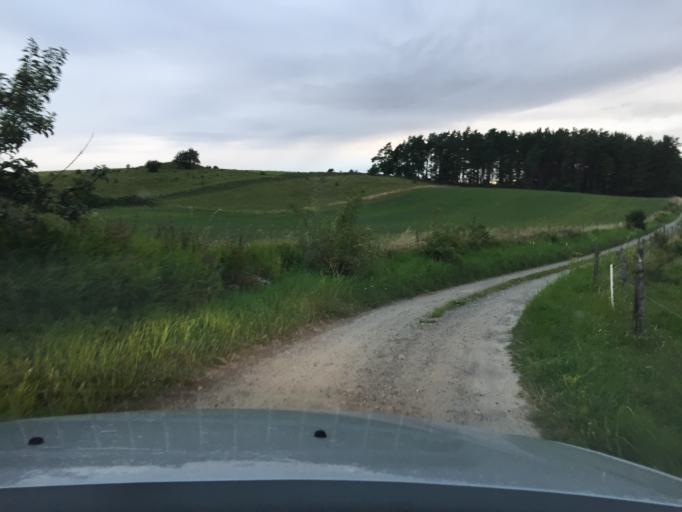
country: SE
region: Skane
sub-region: Kristianstads Kommun
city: Degeberga
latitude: 55.7217
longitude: 14.1272
